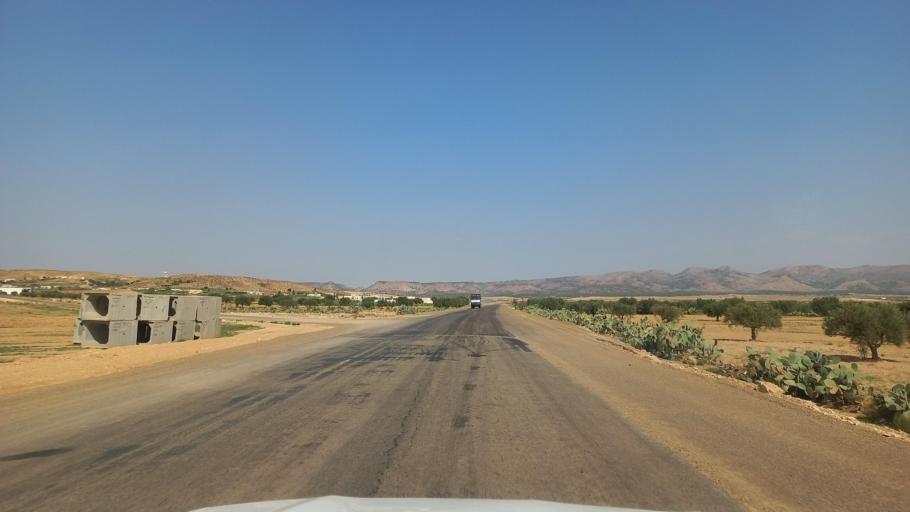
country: TN
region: Al Qasrayn
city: Sbiba
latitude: 35.3769
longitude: 9.0324
